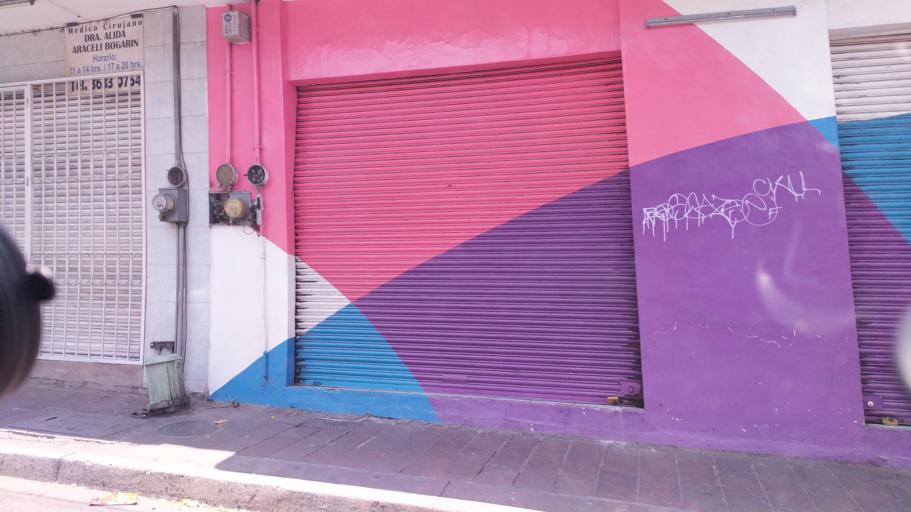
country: MX
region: Jalisco
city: Zapopan2
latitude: 20.7228
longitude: -103.3971
